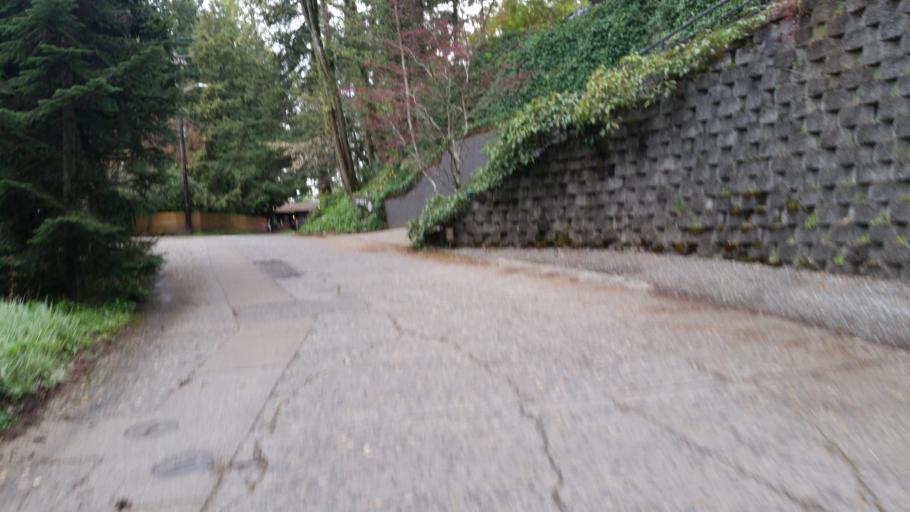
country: US
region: Oregon
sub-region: Multnomah County
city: Portland
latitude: 45.4825
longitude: -122.6879
